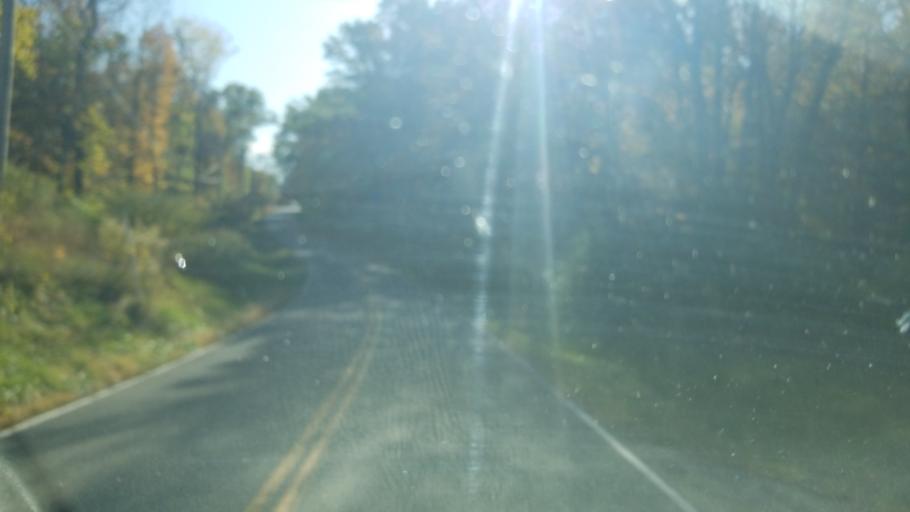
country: US
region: Ohio
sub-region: Warren County
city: Morrow
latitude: 39.4197
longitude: -84.0841
